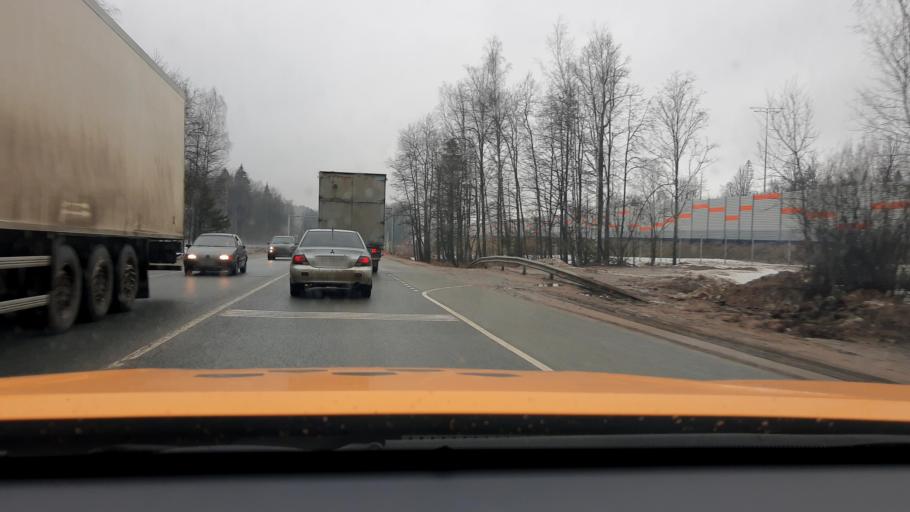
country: RU
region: Moskovskaya
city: Zelenogradskiy
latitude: 56.0967
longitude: 37.9777
